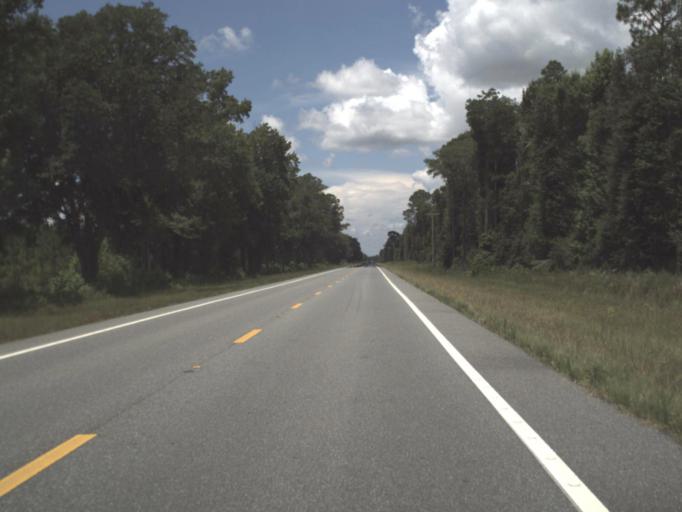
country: US
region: Florida
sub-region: Taylor County
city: Perry
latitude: 30.1428
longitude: -83.8187
